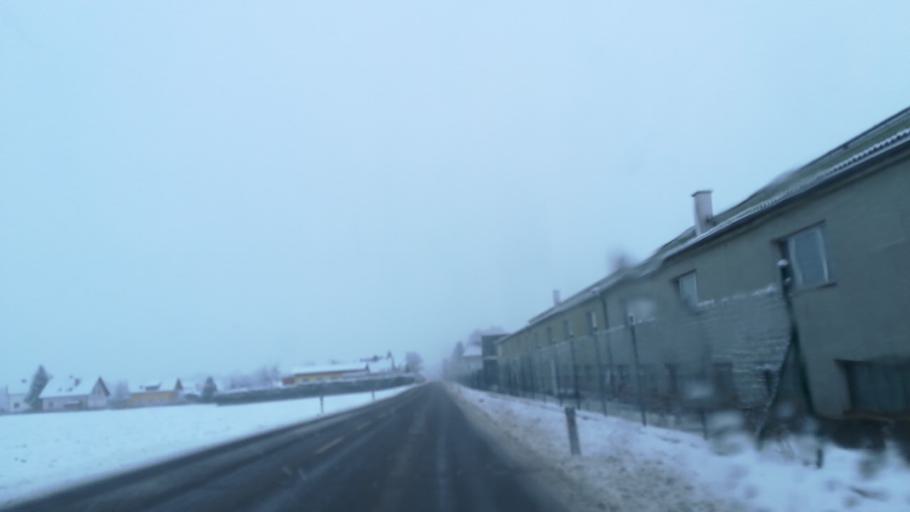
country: AT
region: Styria
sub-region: Politischer Bezirk Murtal
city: Knittelfeld
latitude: 47.2186
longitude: 14.8124
